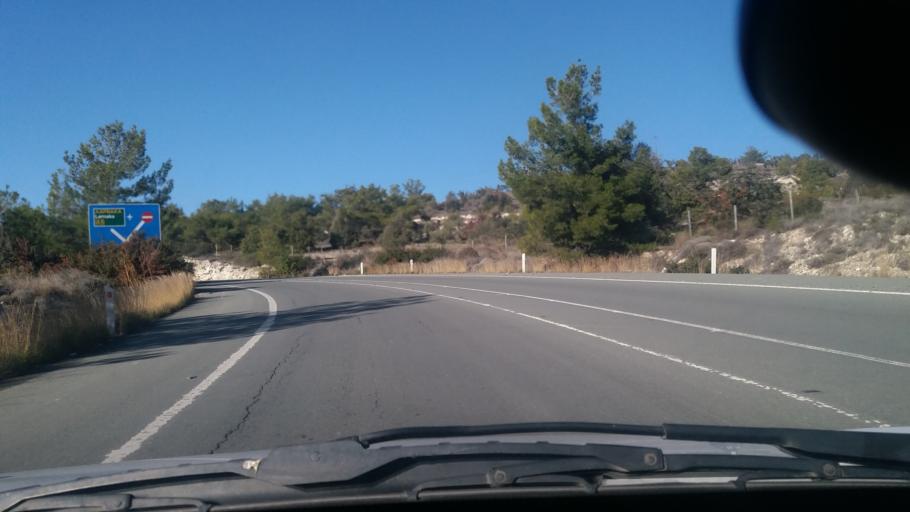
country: CY
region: Larnaka
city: Kofinou
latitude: 34.8546
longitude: 33.4476
